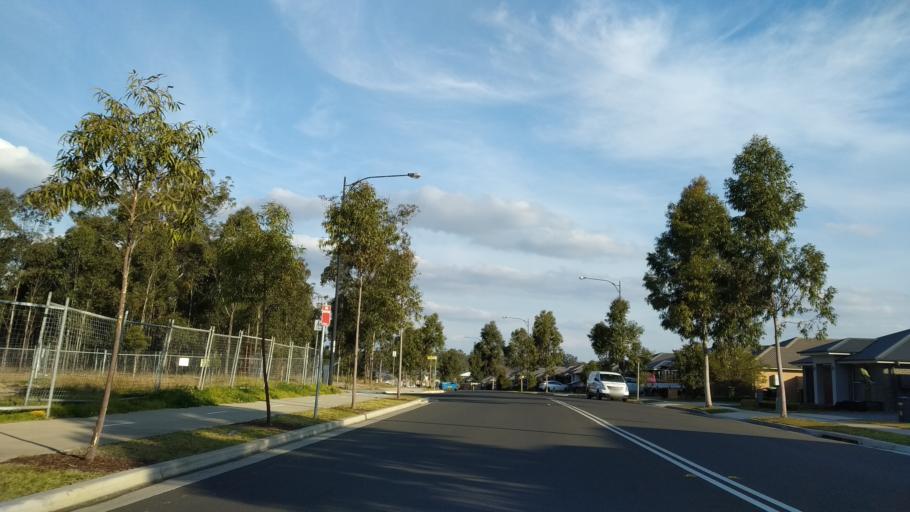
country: AU
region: New South Wales
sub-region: Penrith Municipality
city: Werrington Downs
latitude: -33.7230
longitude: 150.7356
